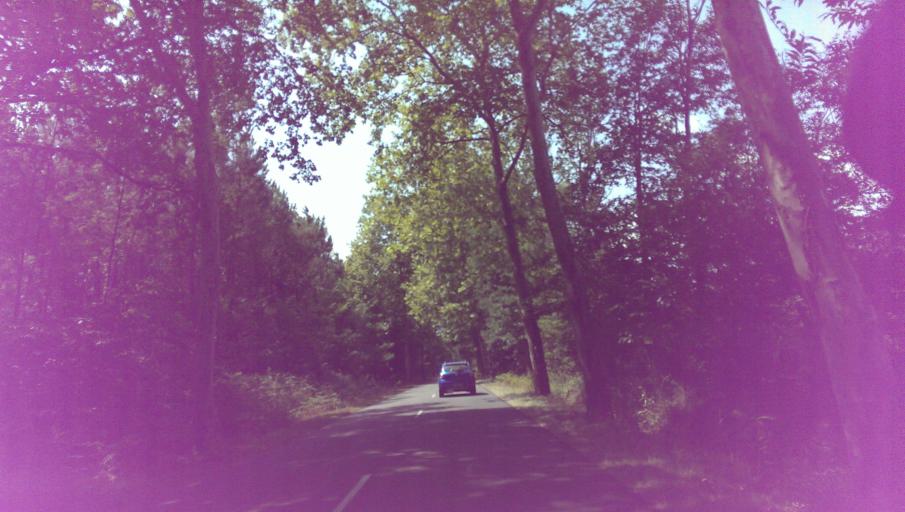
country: FR
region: Aquitaine
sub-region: Departement des Landes
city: Sabres
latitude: 44.1109
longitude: -0.5839
